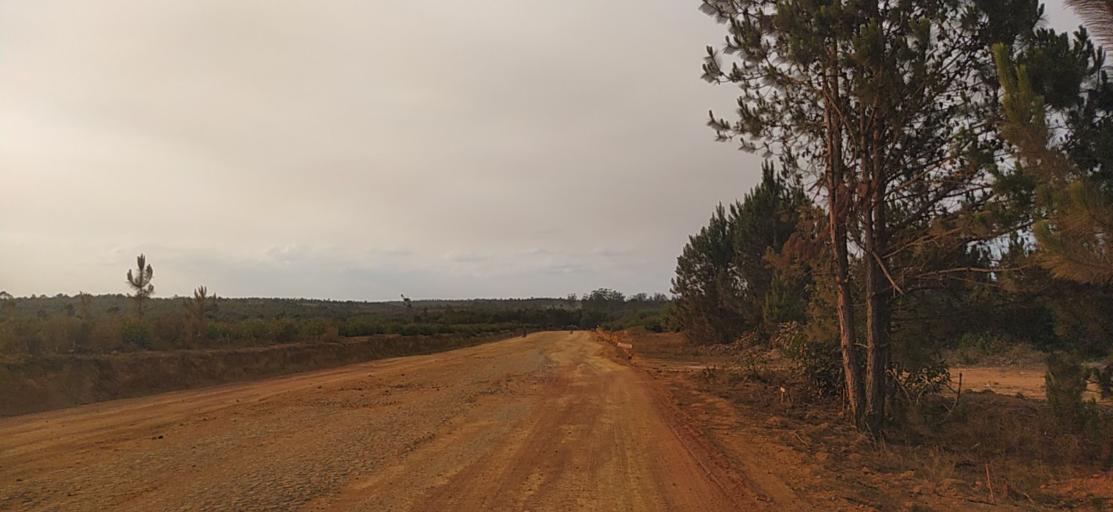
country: MG
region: Alaotra Mangoro
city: Moramanga
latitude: -18.5979
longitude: 48.2781
